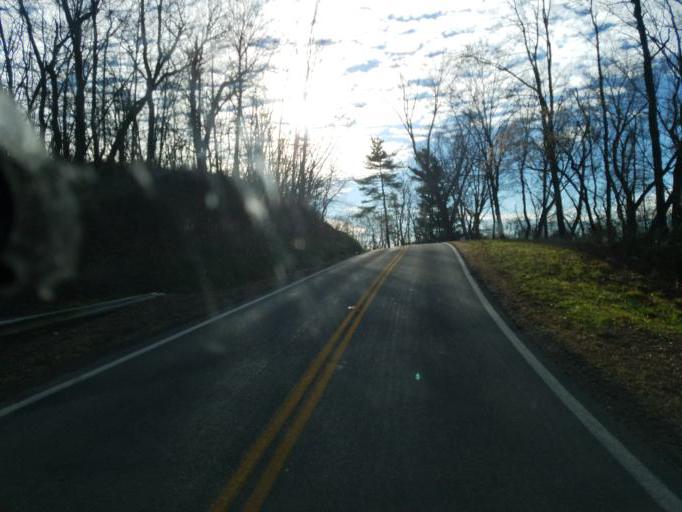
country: US
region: Ohio
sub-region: Muskingum County
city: Dresden
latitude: 40.1168
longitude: -81.9985
